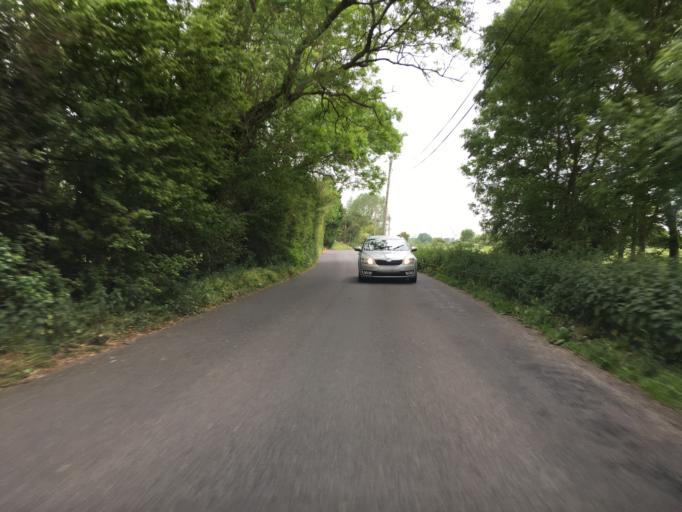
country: GB
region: England
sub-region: North Somerset
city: Kenn
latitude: 51.4237
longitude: -2.8209
